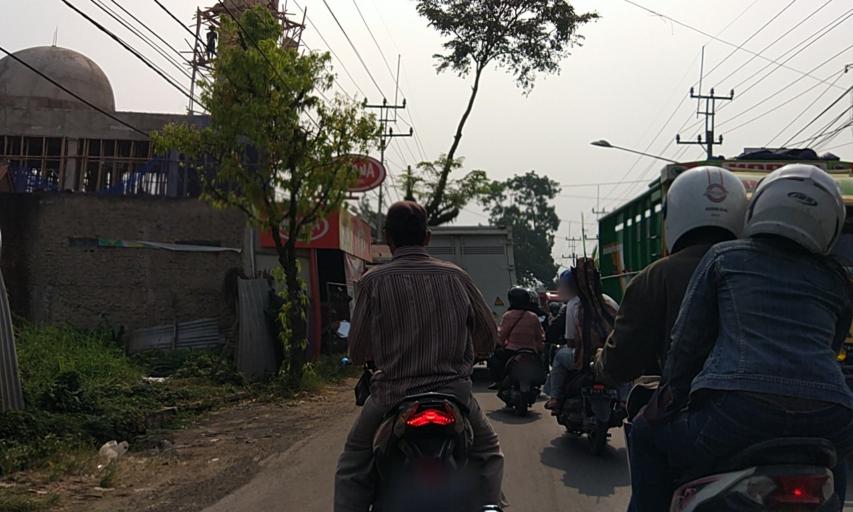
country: ID
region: West Java
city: Banjaran
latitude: -7.0422
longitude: 107.5542
